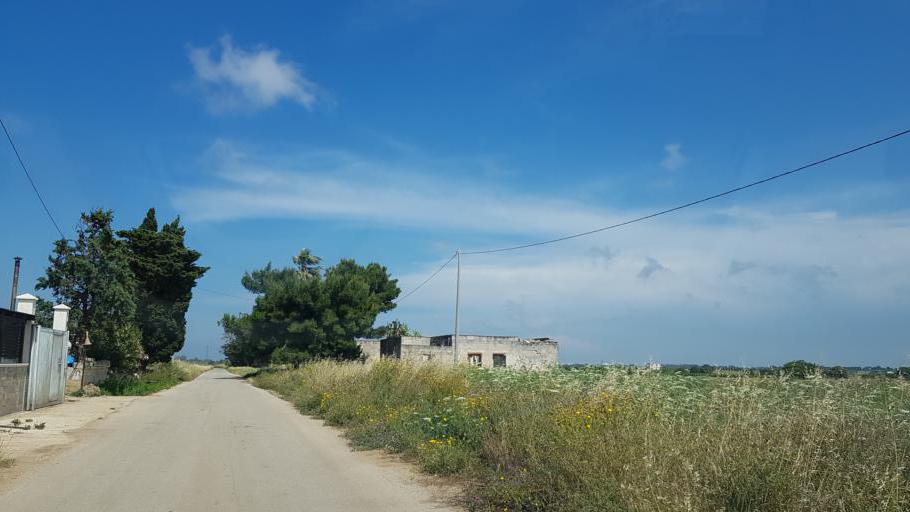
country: IT
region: Apulia
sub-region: Provincia di Brindisi
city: Brindisi
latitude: 40.6609
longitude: 17.8570
